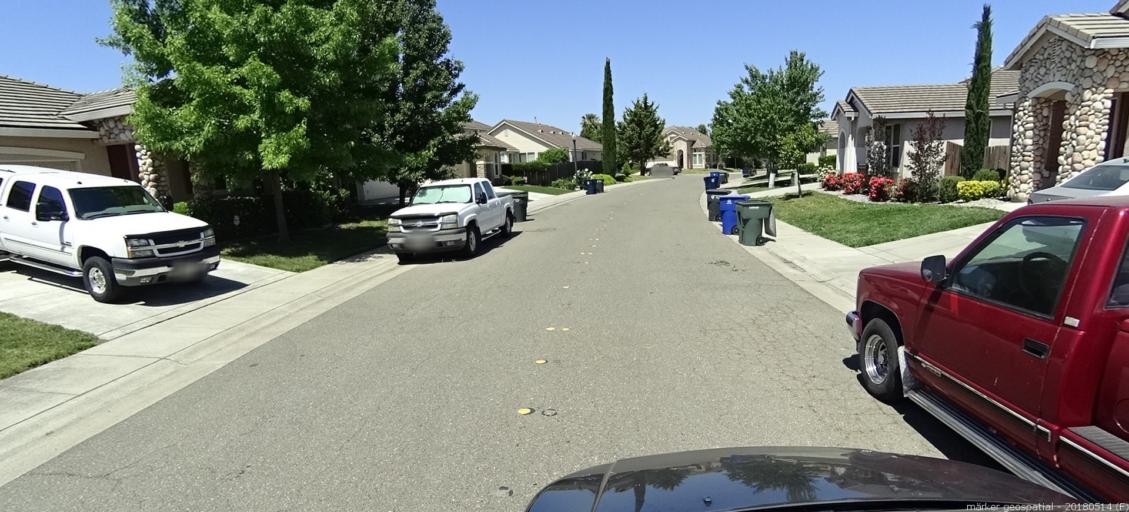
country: US
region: California
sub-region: Yolo County
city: West Sacramento
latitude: 38.6249
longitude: -121.5272
